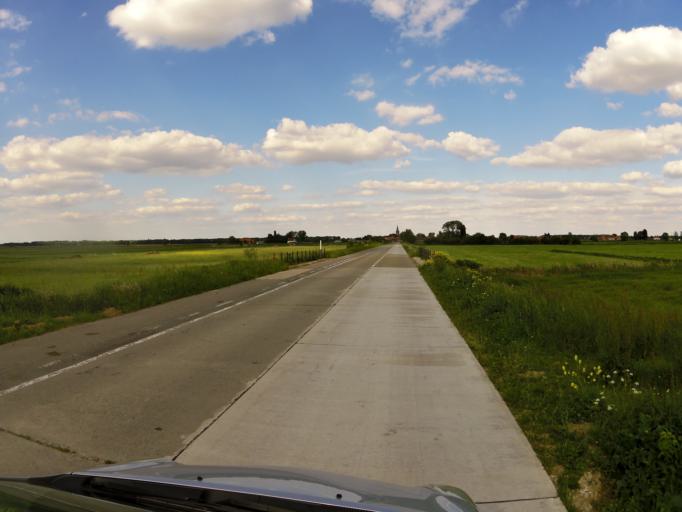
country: BE
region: Flanders
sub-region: Provincie West-Vlaanderen
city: Diksmuide
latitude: 50.9506
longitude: 2.7975
